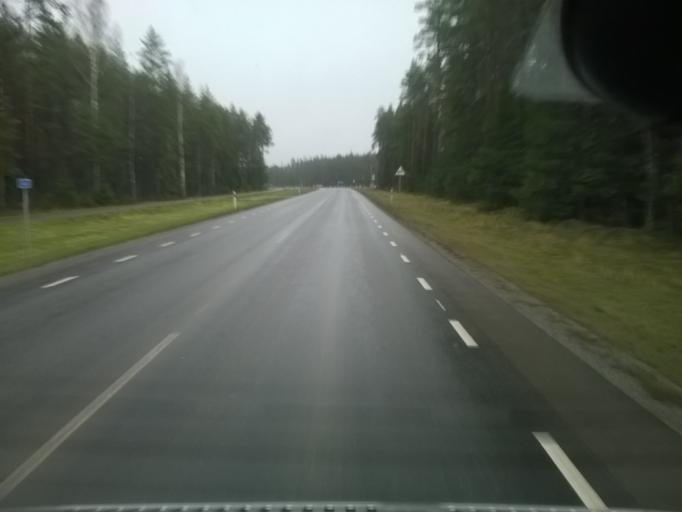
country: EE
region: Harju
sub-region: Saku vald
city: Saku
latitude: 59.2493
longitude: 24.6848
